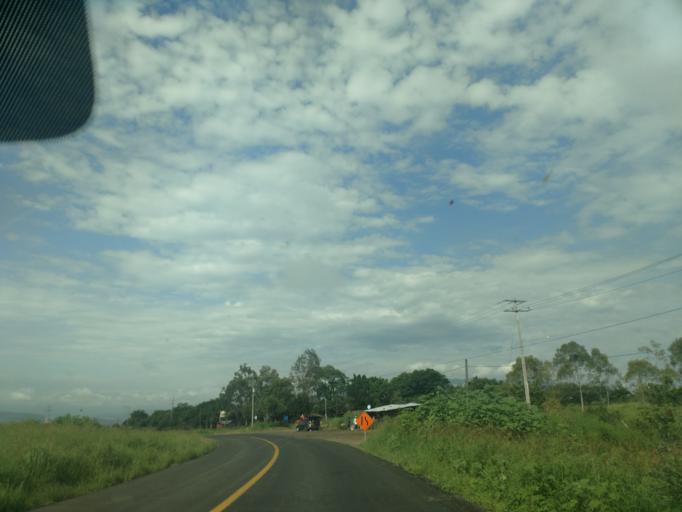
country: MX
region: Jalisco
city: El Salto
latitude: 20.4358
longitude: -104.4481
